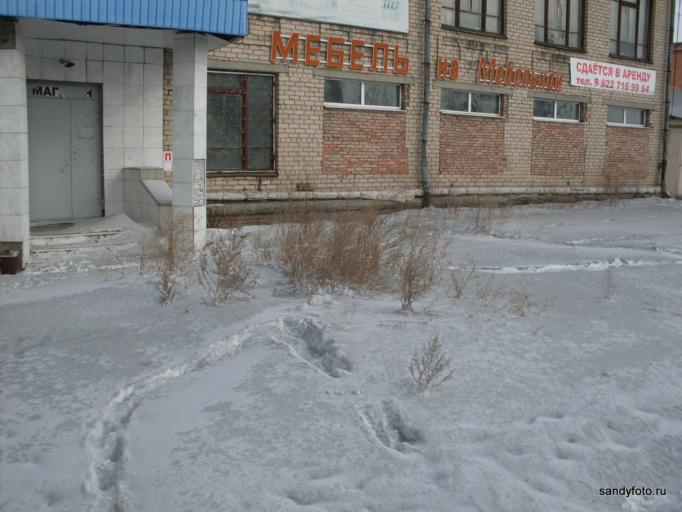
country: RU
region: Chelyabinsk
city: Troitsk
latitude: 54.0415
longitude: 61.6387
